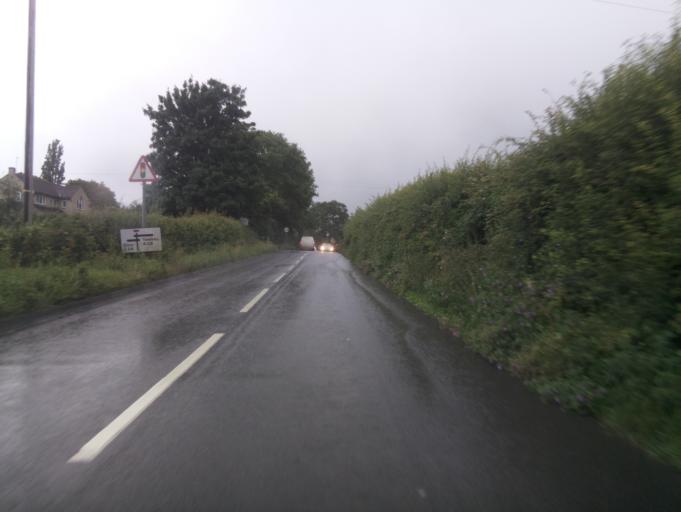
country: GB
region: England
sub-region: Gloucestershire
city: Tewkesbury
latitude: 51.9665
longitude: -2.1560
